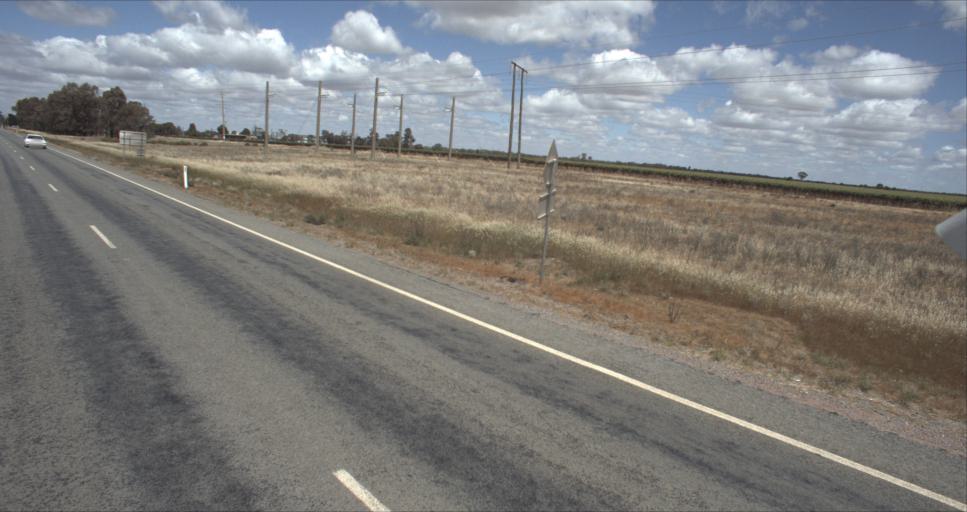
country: AU
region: New South Wales
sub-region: Murrumbidgee Shire
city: Darlington Point
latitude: -34.5048
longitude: 146.1874
